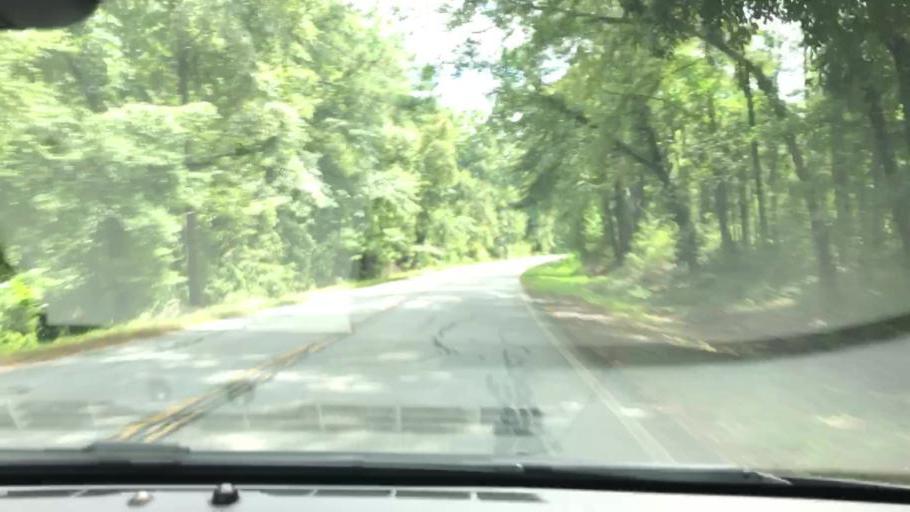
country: US
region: Georgia
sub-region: Quitman County
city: Georgetown
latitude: 32.0385
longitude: -85.0287
